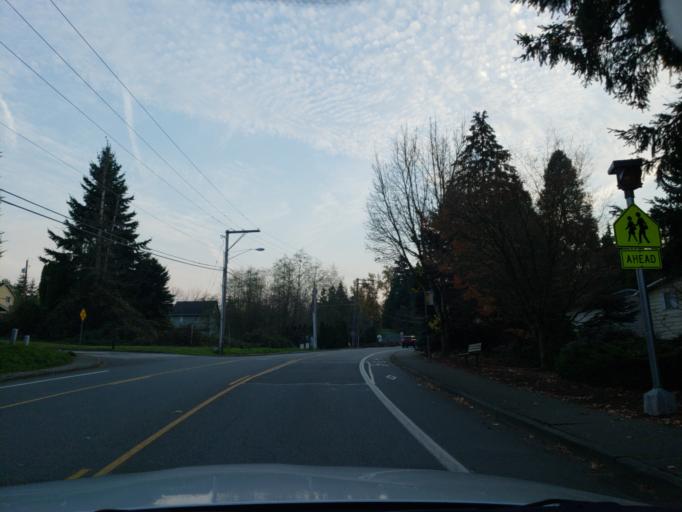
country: US
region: Washington
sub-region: King County
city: Woodinville
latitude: 47.7517
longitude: -122.1793
